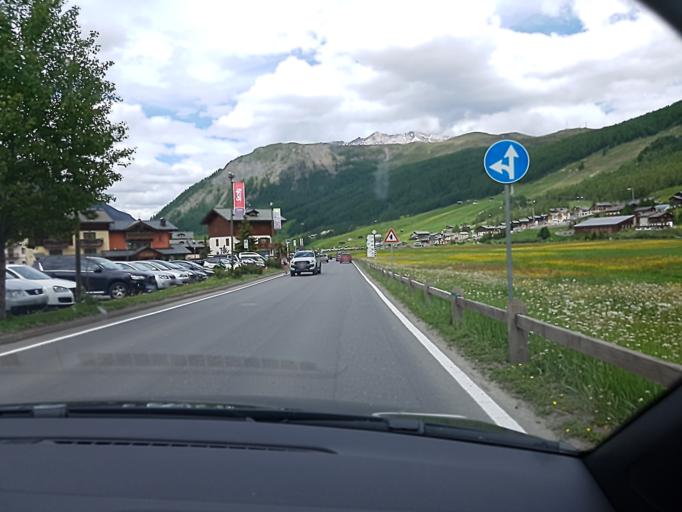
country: IT
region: Lombardy
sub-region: Provincia di Sondrio
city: Livigno
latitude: 46.5333
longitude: 10.1335
